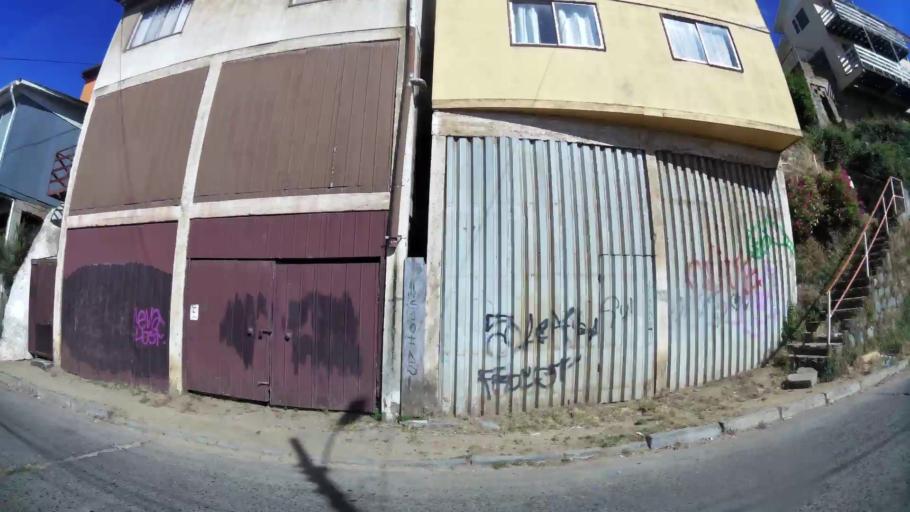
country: CL
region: Valparaiso
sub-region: Provincia de Valparaiso
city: Valparaiso
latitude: -33.0445
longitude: -71.6349
